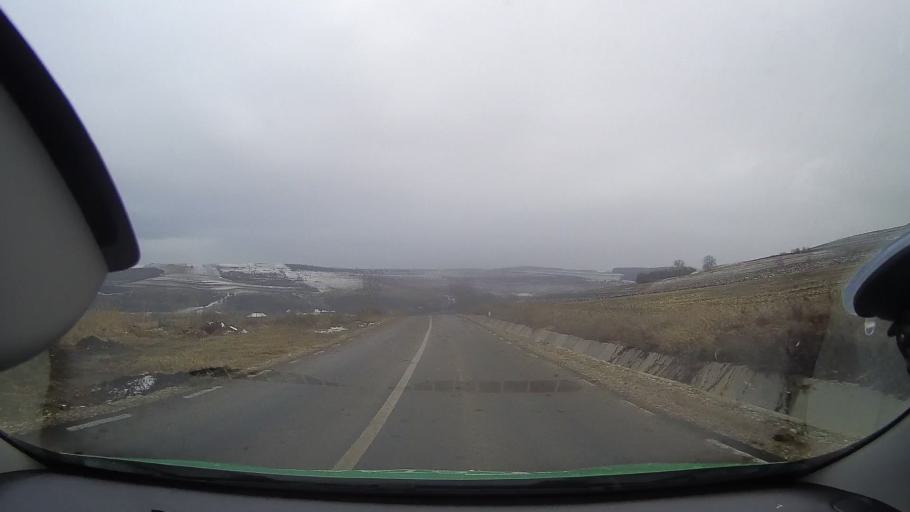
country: RO
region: Alba
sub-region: Comuna Farau
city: Farau
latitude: 46.3917
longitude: 24.0204
